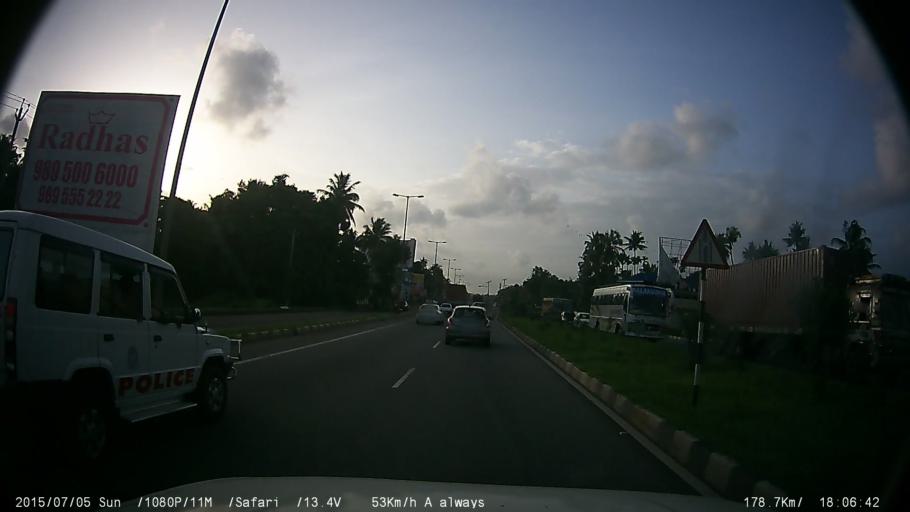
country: IN
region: Kerala
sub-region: Thrissur District
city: Kizhake Chalakudi
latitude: 10.3176
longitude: 76.3275
